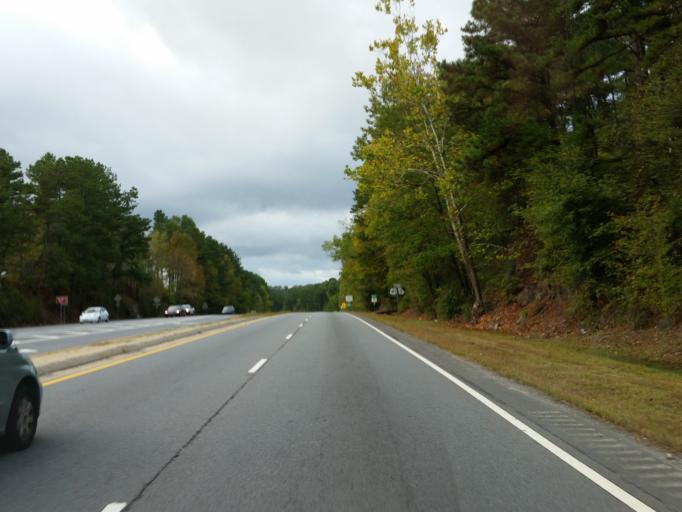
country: US
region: Georgia
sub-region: Cobb County
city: Acworth
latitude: 34.0777
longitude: -84.7286
